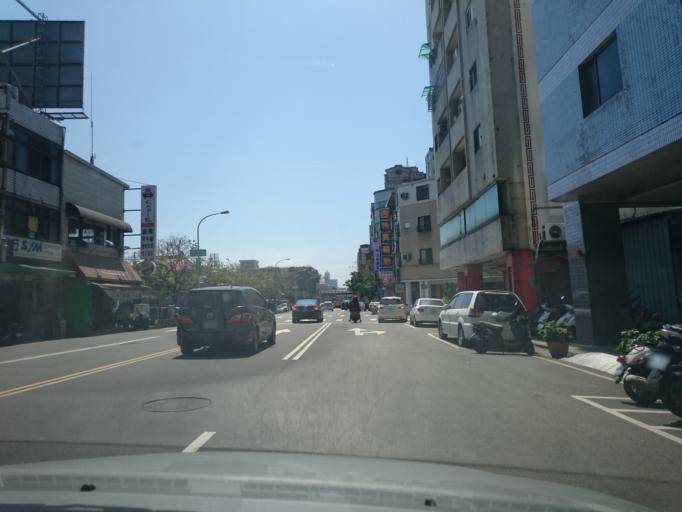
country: TW
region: Taiwan
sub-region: Taichung City
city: Taichung
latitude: 24.1558
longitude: 120.6900
